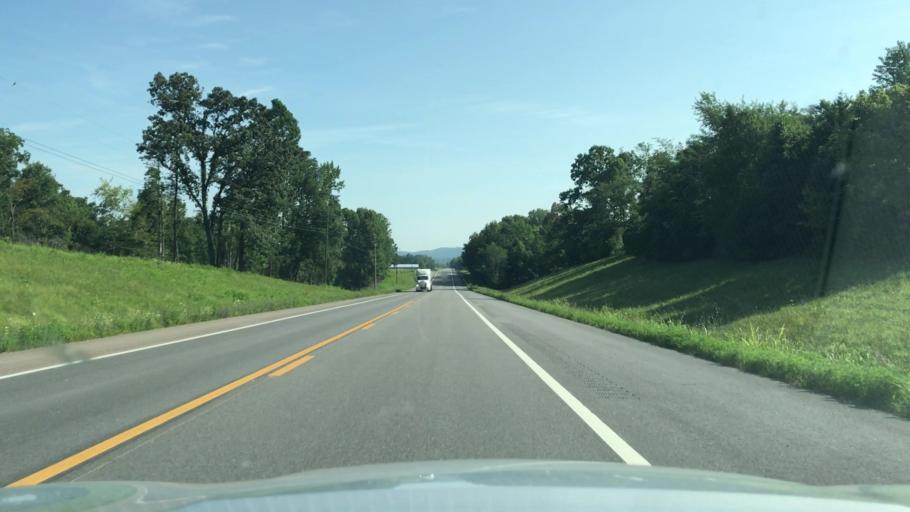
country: US
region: Tennessee
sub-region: Pickett County
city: Byrdstown
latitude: 36.5048
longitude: -85.1751
